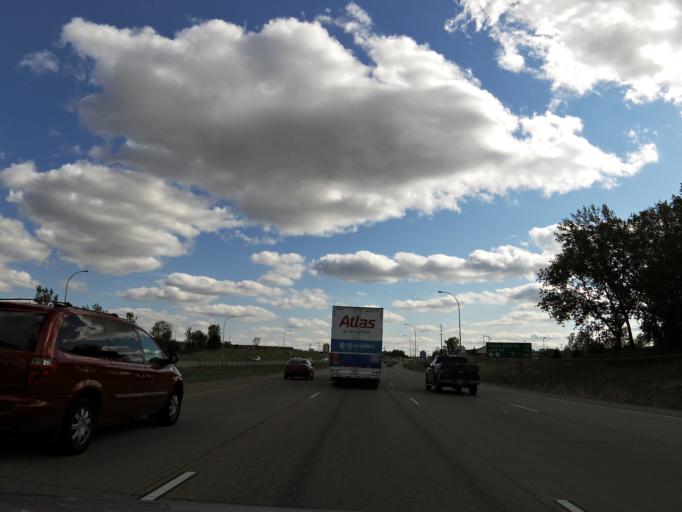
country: US
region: Minnesota
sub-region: Washington County
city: Woodbury
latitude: 44.9341
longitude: -92.9617
